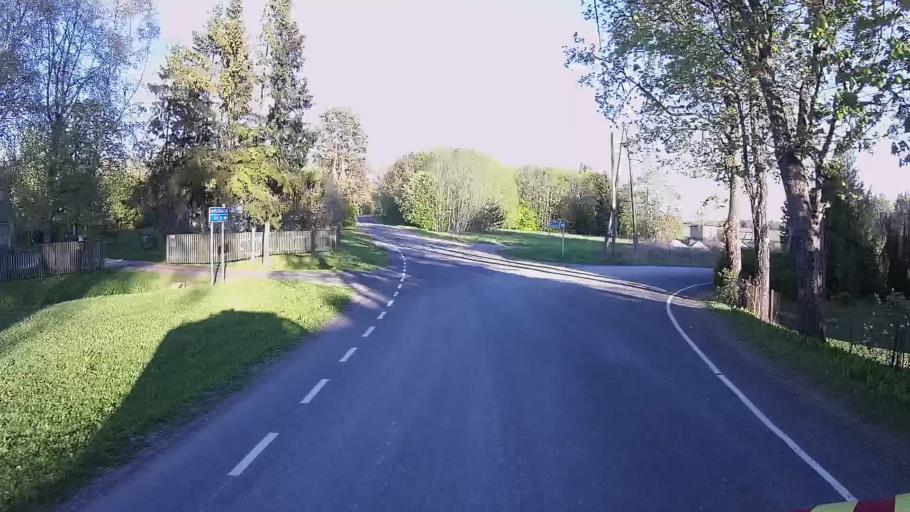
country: EE
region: Jogevamaa
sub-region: Poltsamaa linn
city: Poltsamaa
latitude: 58.5269
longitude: 25.9542
